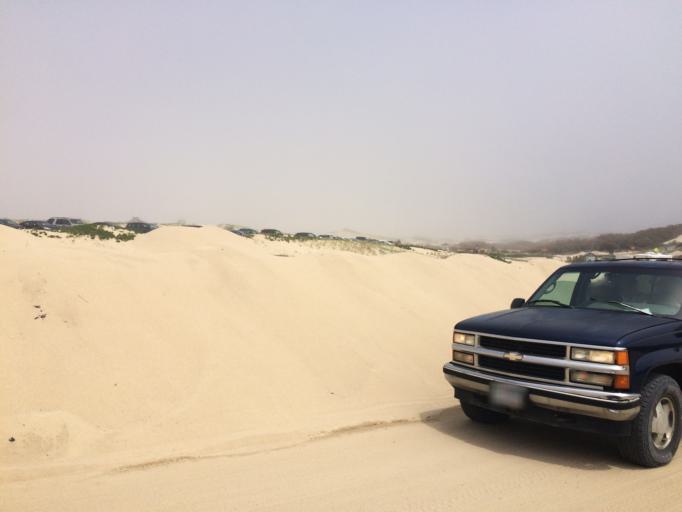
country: US
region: Massachusetts
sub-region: Barnstable County
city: Provincetown
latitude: 42.0780
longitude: -70.2200
